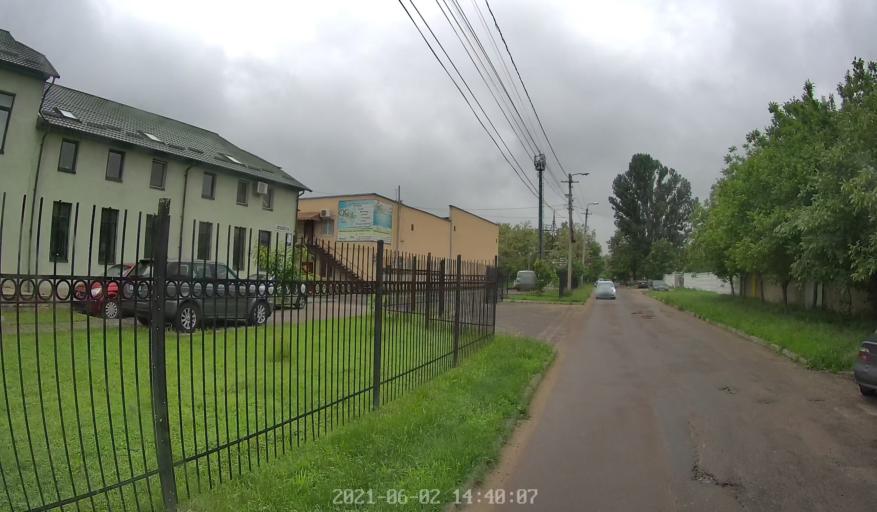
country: MD
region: Chisinau
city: Chisinau
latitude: 47.0449
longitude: 28.8010
